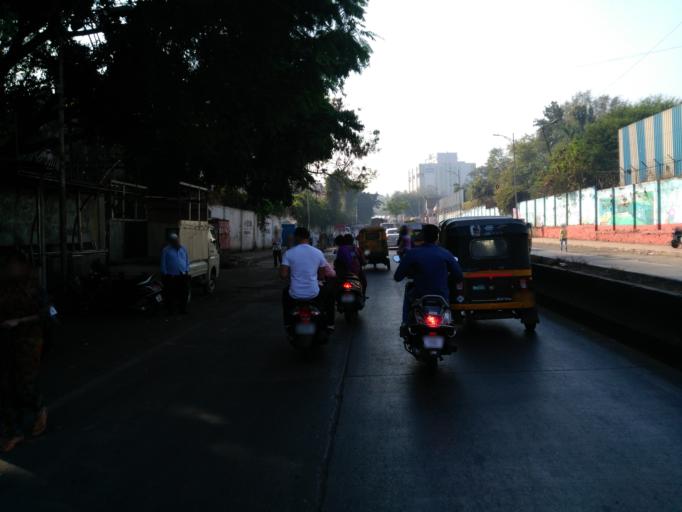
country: IN
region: Maharashtra
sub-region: Pune Division
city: Pune
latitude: 18.4959
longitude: 73.8693
